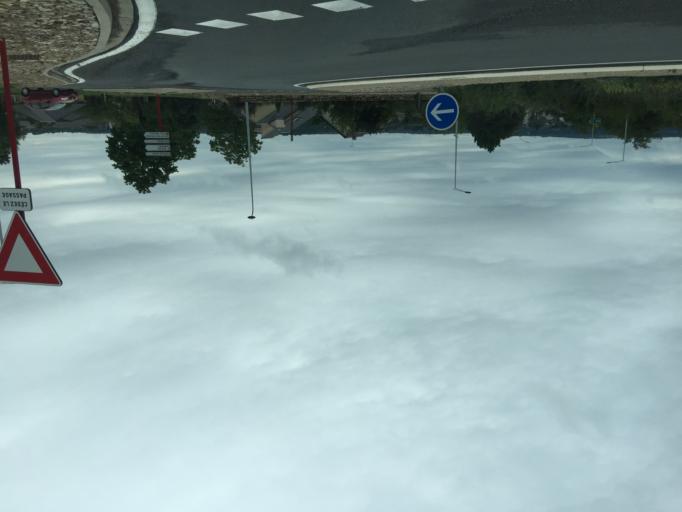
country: FR
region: Midi-Pyrenees
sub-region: Departement de l'Aveyron
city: Bozouls
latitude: 44.4748
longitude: 2.7308
